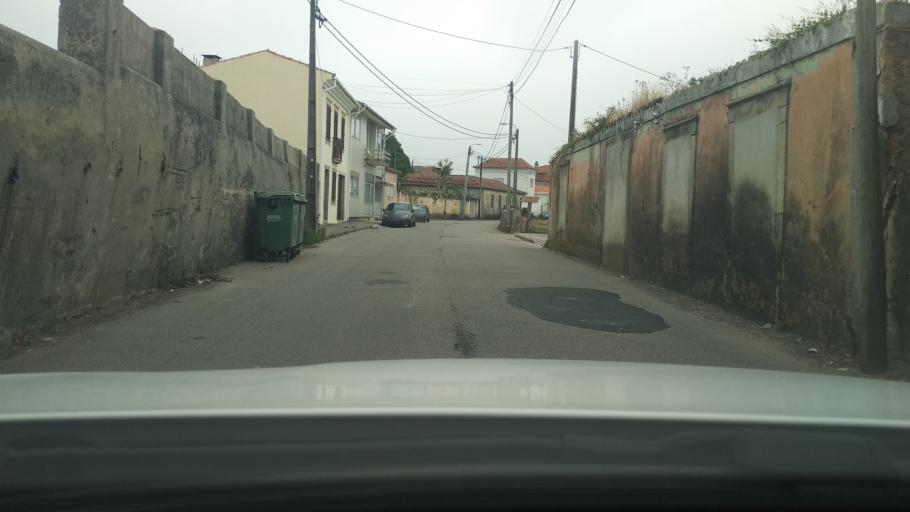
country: PT
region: Aveiro
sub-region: Espinho
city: Silvalde
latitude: 40.9915
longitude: -8.6257
